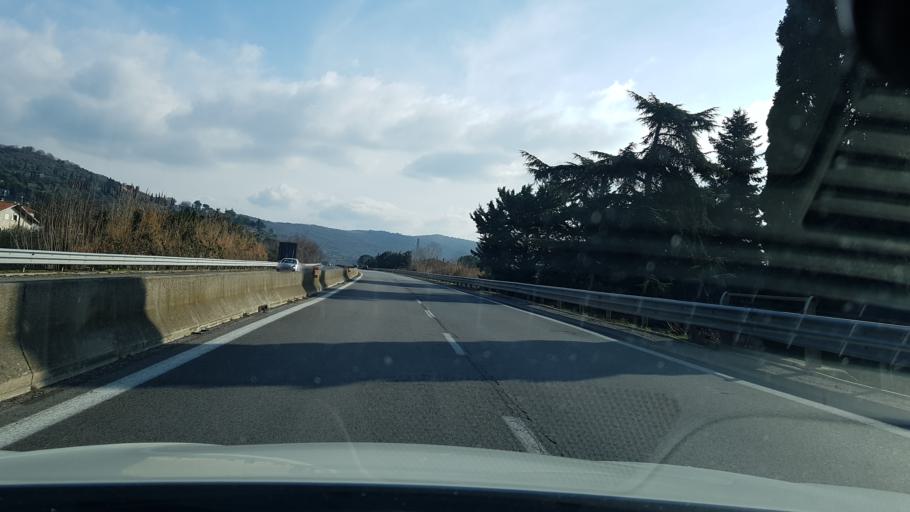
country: IT
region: Umbria
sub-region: Provincia di Perugia
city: Passignano sul Trasimeno
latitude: 43.1837
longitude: 12.1619
